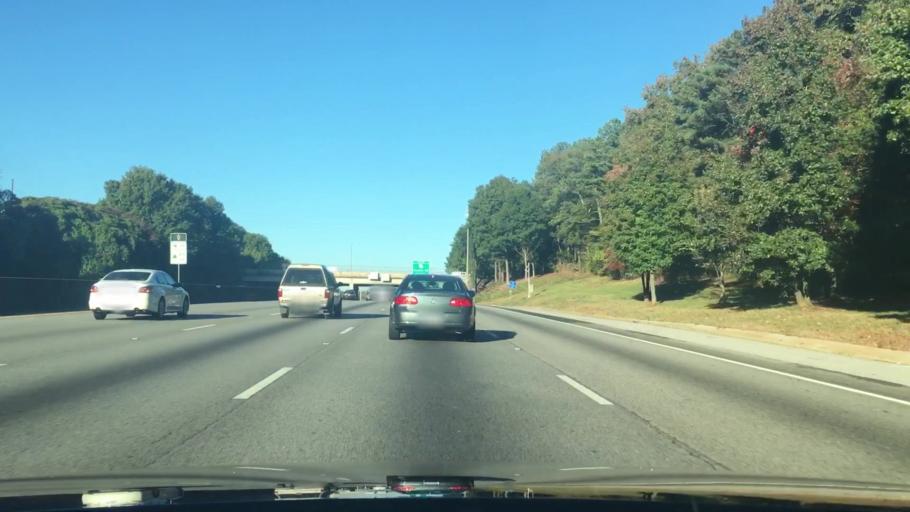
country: US
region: Georgia
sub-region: DeKalb County
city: Panthersville
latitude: 33.7155
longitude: -84.2515
